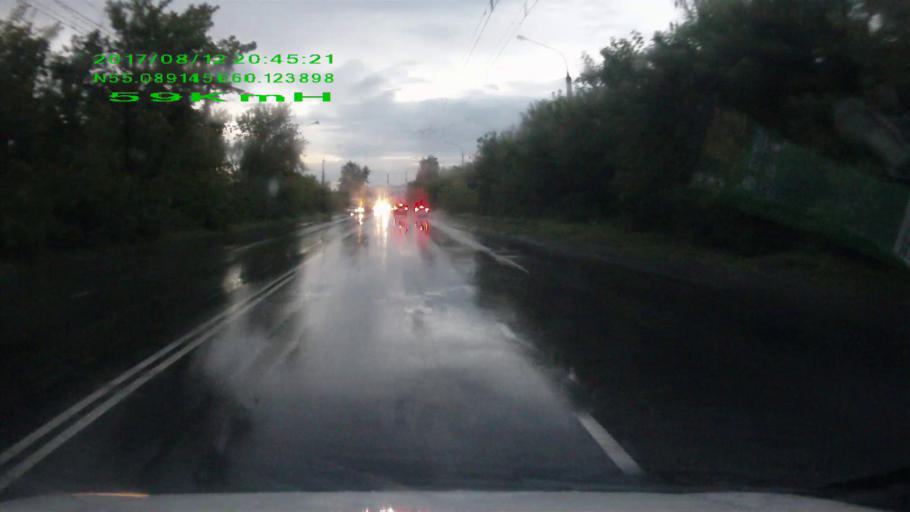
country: RU
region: Chelyabinsk
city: Miass
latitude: 55.0891
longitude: 60.1239
